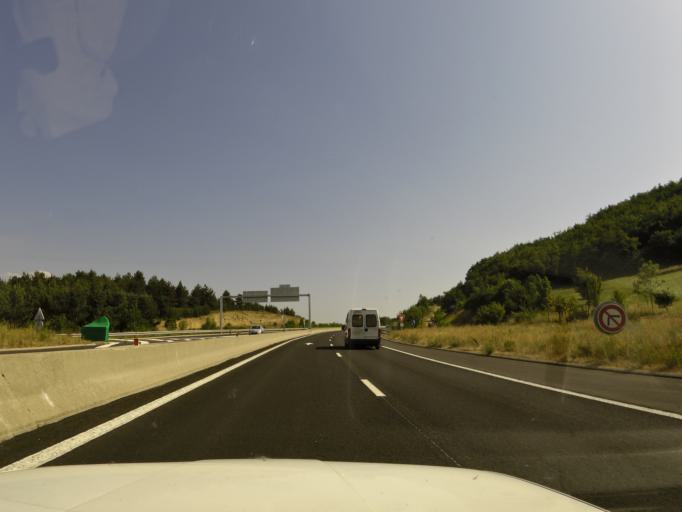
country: FR
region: Languedoc-Roussillon
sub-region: Departement de la Lozere
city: Chirac
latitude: 44.5082
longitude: 3.2437
